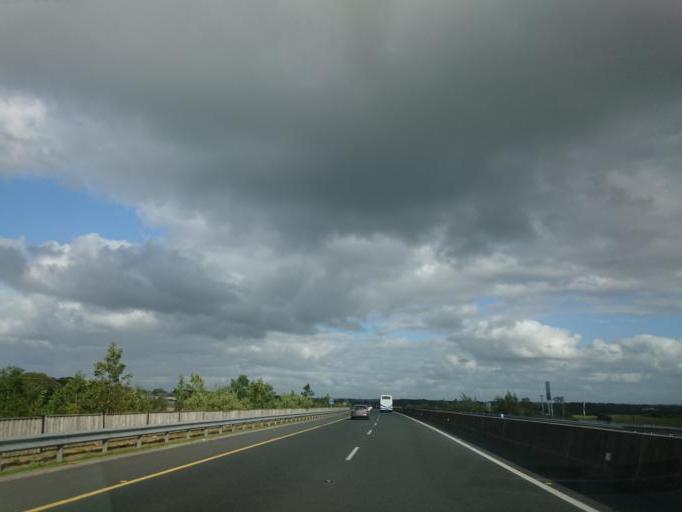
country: IE
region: Connaught
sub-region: County Galway
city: Athenry
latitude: 53.2710
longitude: -8.6732
